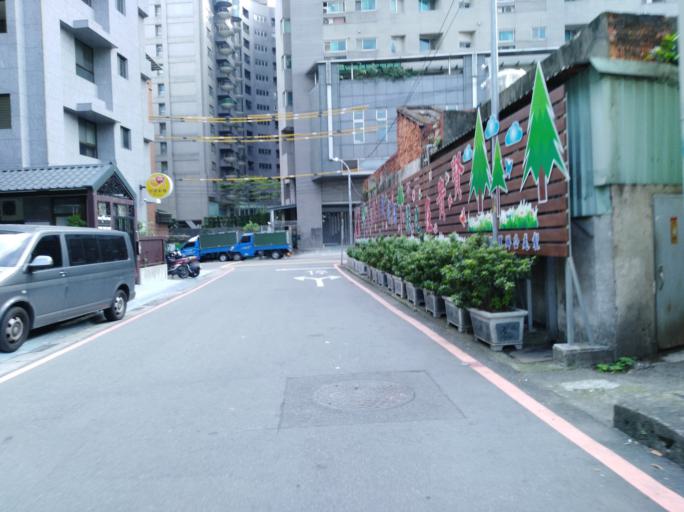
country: TW
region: Taipei
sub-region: Taipei
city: Banqiao
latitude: 25.0424
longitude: 121.4254
